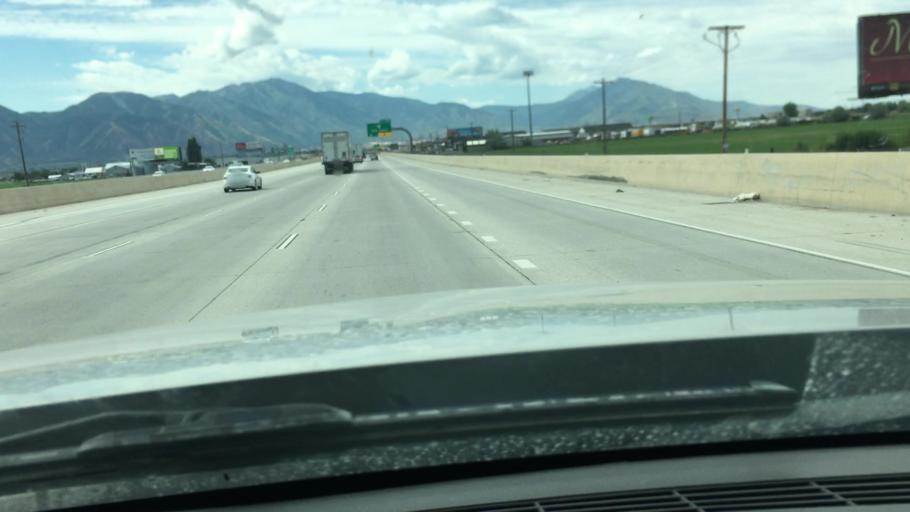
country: US
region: Utah
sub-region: Utah County
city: Springville
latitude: 40.1740
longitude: -111.6469
